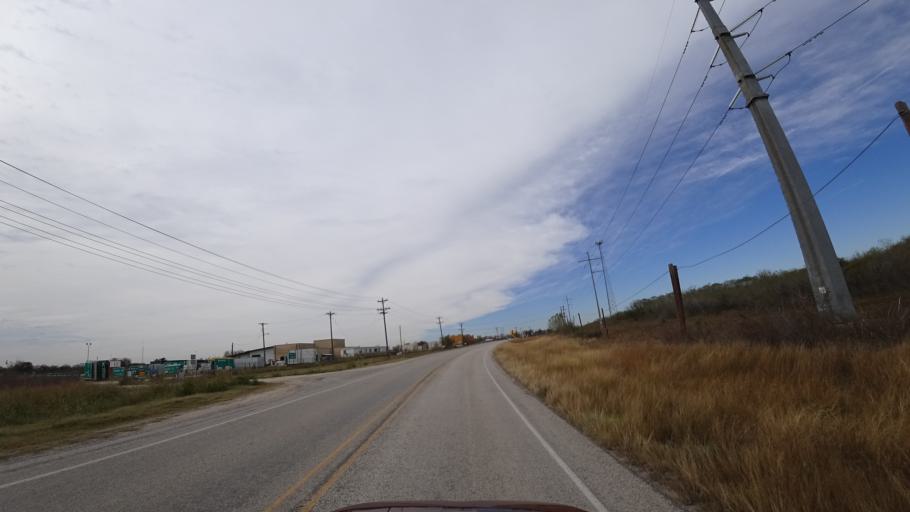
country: US
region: Texas
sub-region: Travis County
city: Garfield
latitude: 30.1390
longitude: -97.5637
